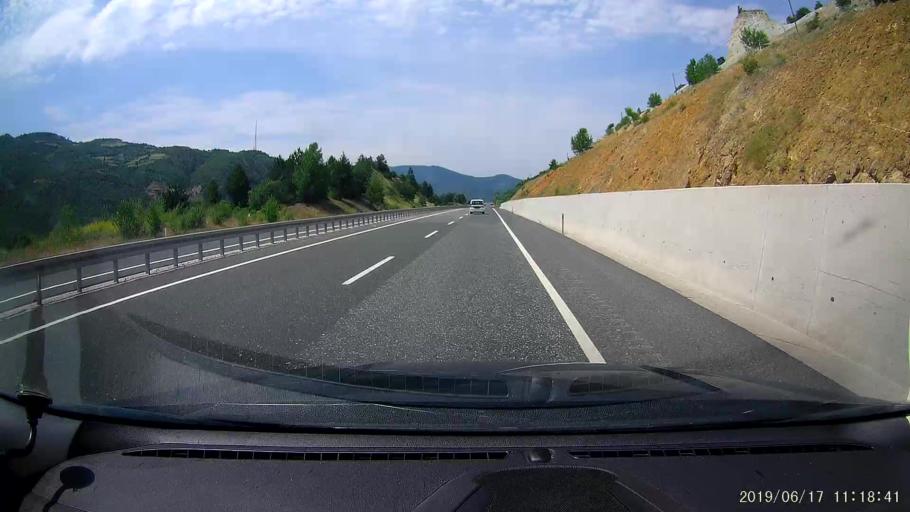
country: TR
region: Cankiri
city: Yaprakli
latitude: 40.9318
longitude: 33.8449
